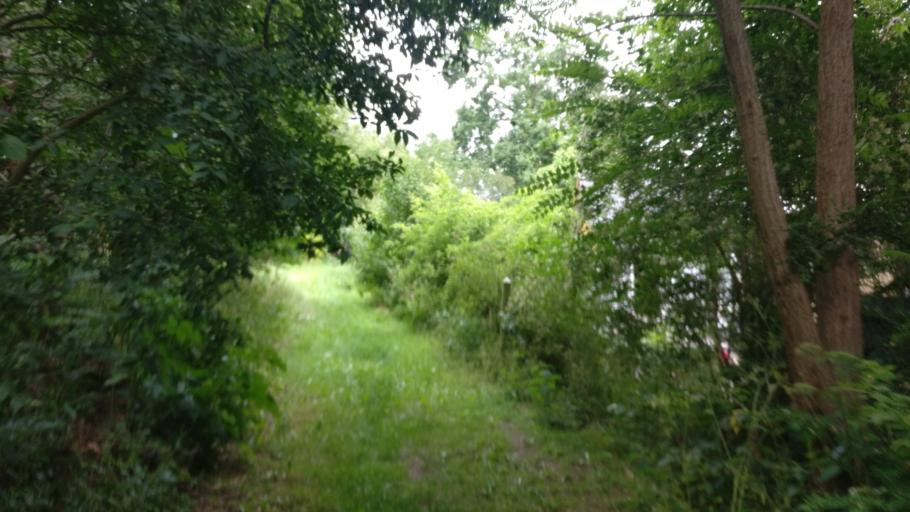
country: DK
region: Capital Region
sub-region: Egedal Kommune
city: Vekso
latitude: 55.7576
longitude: 12.2272
